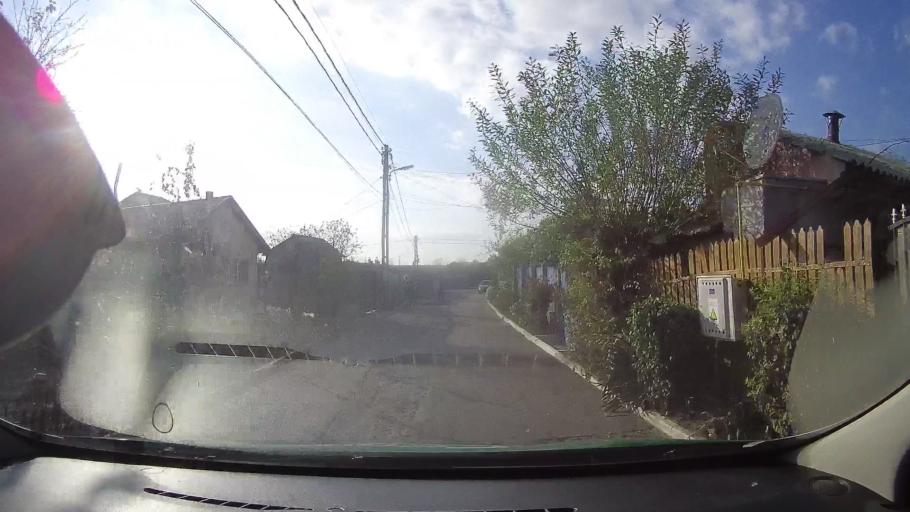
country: RO
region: Constanta
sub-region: Comuna Lumina
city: Lumina
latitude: 44.2871
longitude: 28.5610
